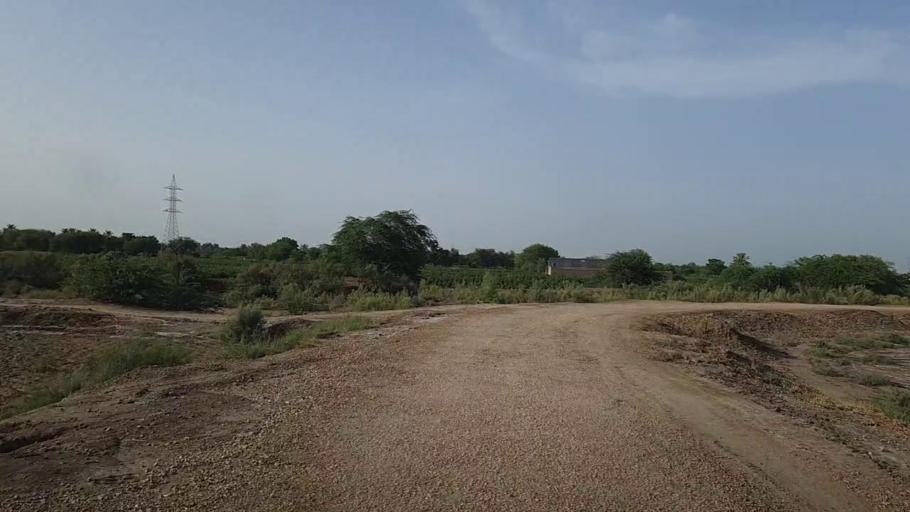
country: PK
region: Sindh
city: Karaundi
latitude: 26.8900
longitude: 68.3060
